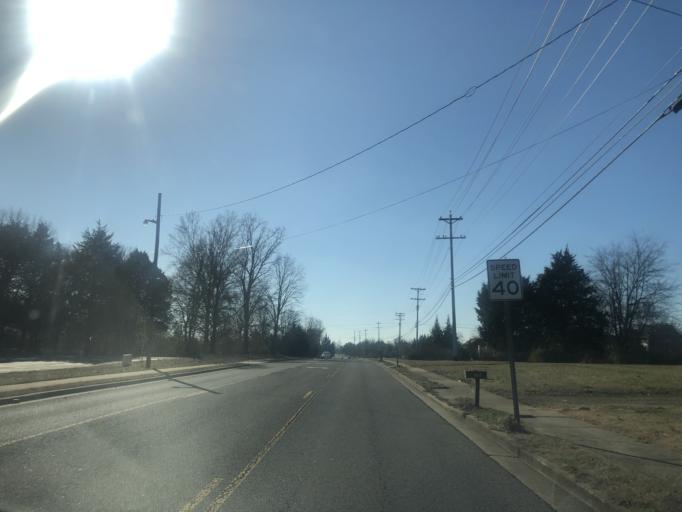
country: US
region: Tennessee
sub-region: Rutherford County
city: Smyrna
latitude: 35.9118
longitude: -86.4715
